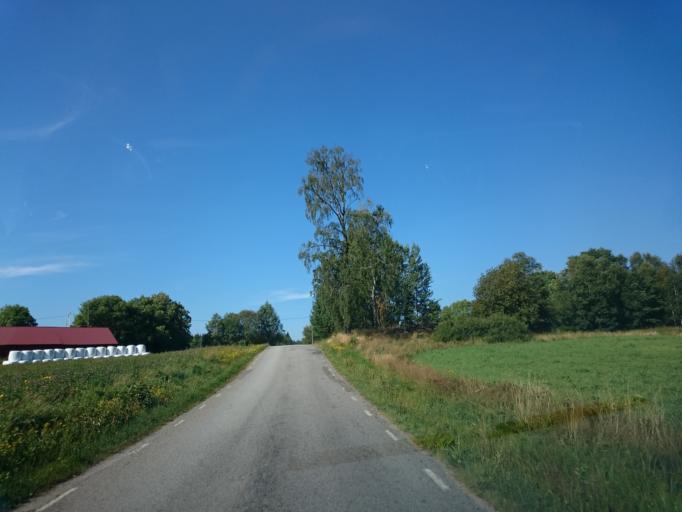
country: SE
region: Soedermanland
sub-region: Nykopings Kommun
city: Olstorp
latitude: 58.6500
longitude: 16.6511
